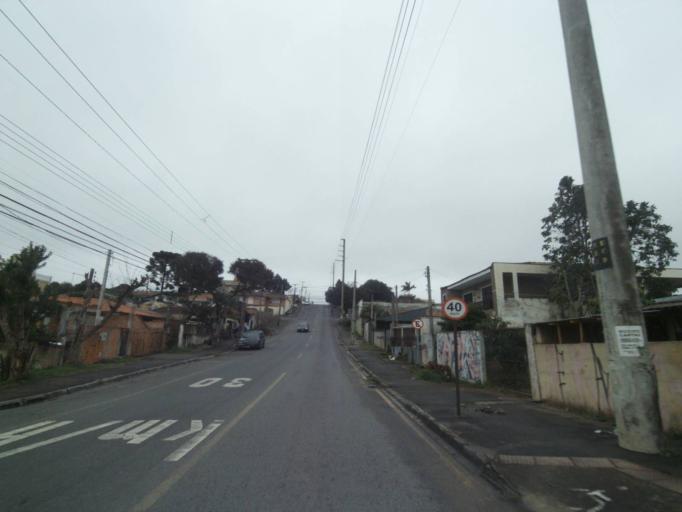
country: BR
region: Parana
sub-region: Curitiba
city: Curitiba
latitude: -25.5068
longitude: -49.3045
